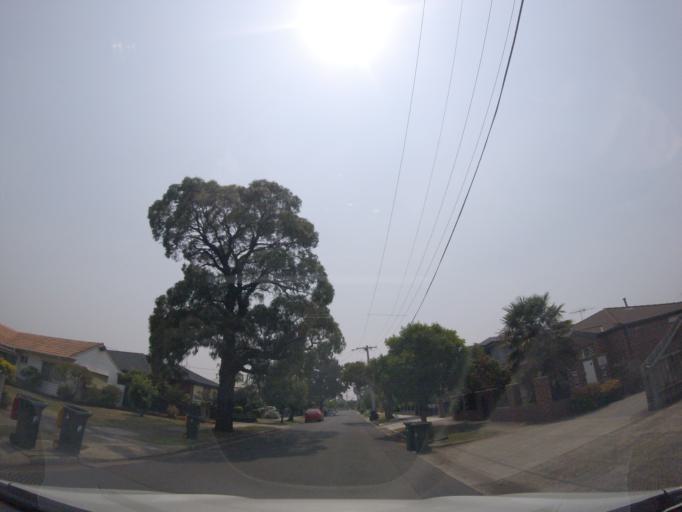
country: AU
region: Victoria
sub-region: Moreland
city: Oak Park
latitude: -37.7220
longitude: 144.9304
